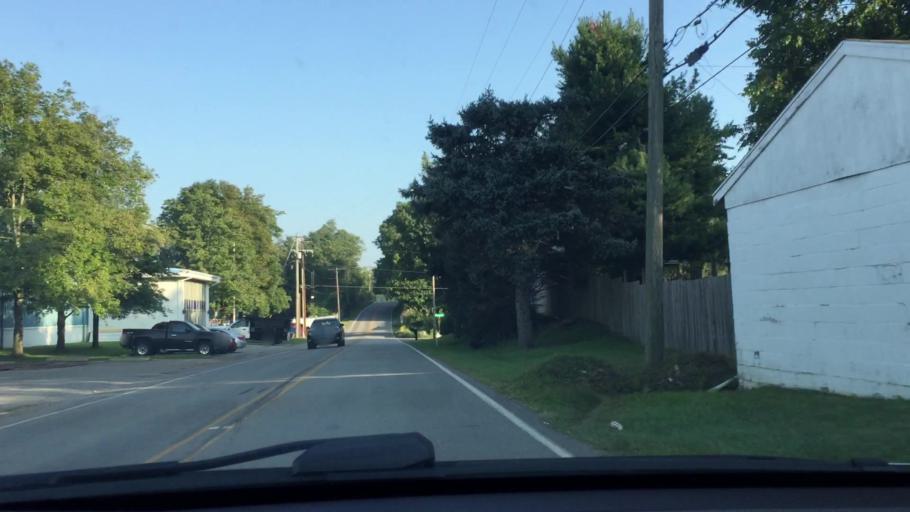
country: US
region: Pennsylvania
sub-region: Washington County
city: East Washington
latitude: 40.1958
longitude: -80.2198
